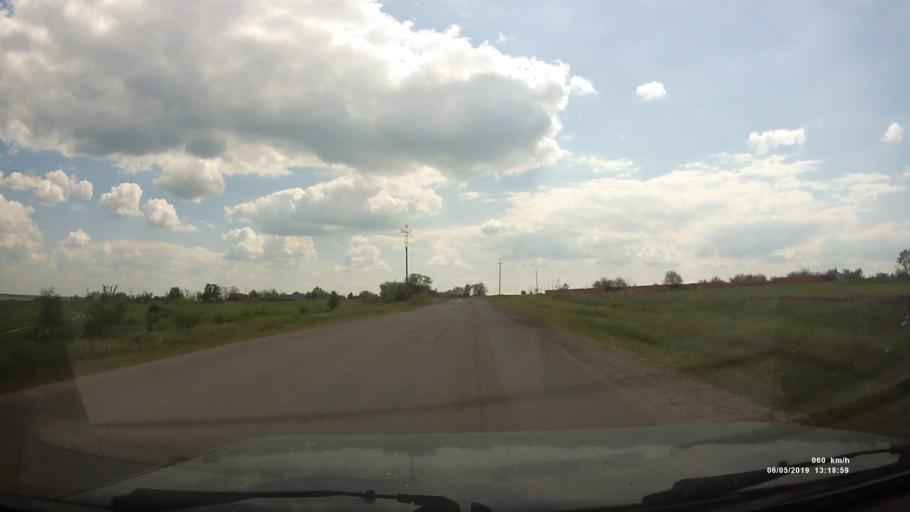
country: RU
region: Rostov
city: Ust'-Donetskiy
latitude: 47.7293
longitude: 40.9140
